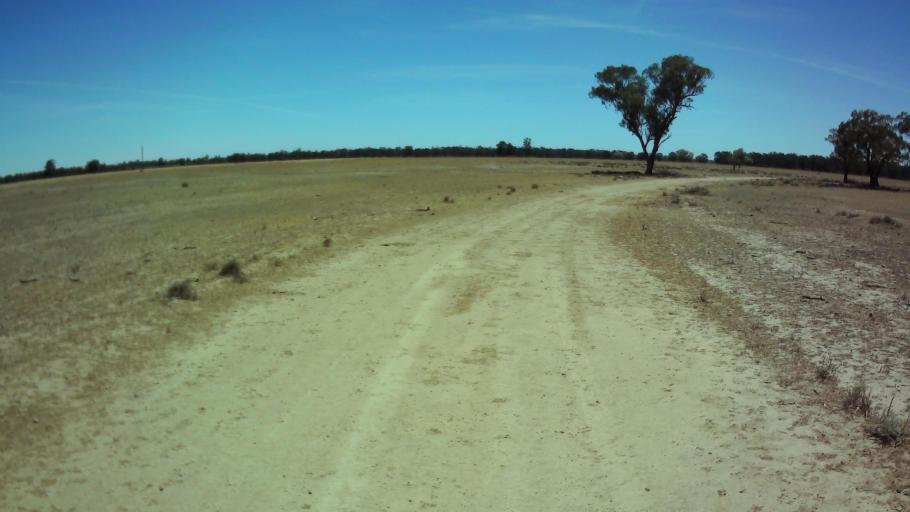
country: AU
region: New South Wales
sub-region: Bland
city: West Wyalong
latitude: -33.8377
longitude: 147.6330
